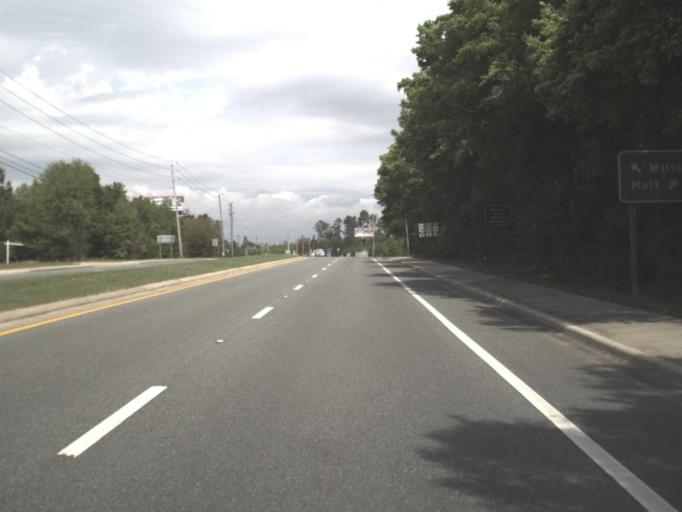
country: US
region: Florida
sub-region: Santa Rosa County
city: East Milton
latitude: 30.6316
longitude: -86.9700
